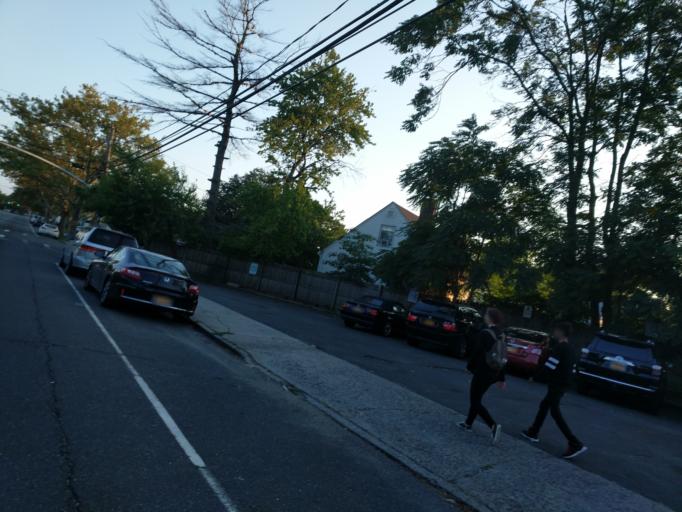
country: US
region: New York
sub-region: Nassau County
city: Valley Stream
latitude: 40.6575
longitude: -73.7096
